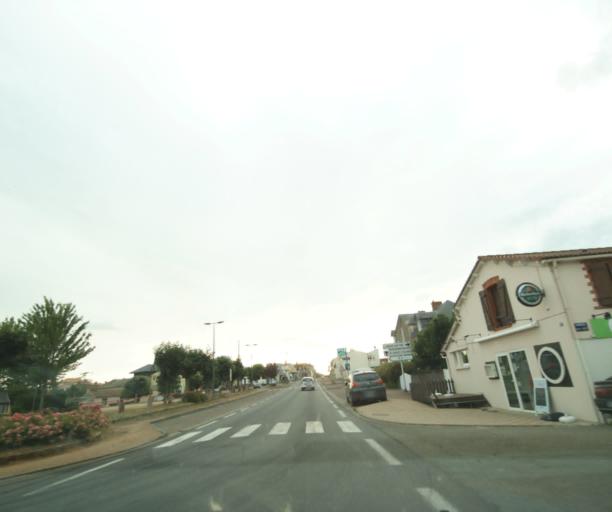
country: FR
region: Pays de la Loire
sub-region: Departement de la Vendee
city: Avrille
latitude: 46.4702
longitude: -1.4913
